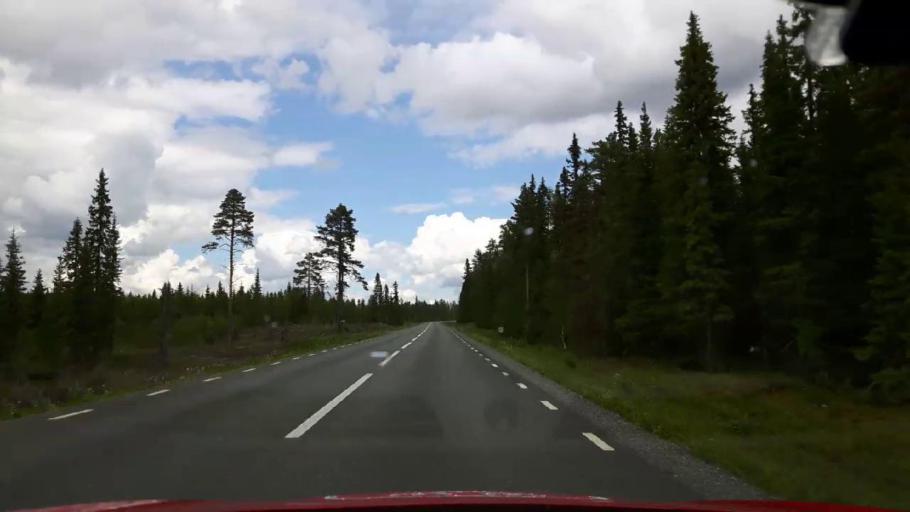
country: SE
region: Jaemtland
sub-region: Krokoms Kommun
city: Krokom
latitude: 63.5760
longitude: 14.2809
